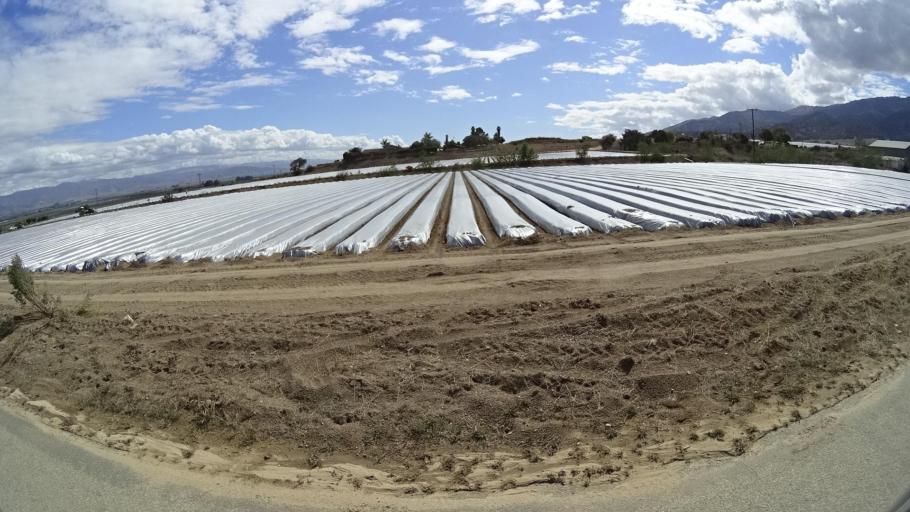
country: US
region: California
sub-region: Monterey County
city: Chualar
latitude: 36.5903
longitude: -121.6073
